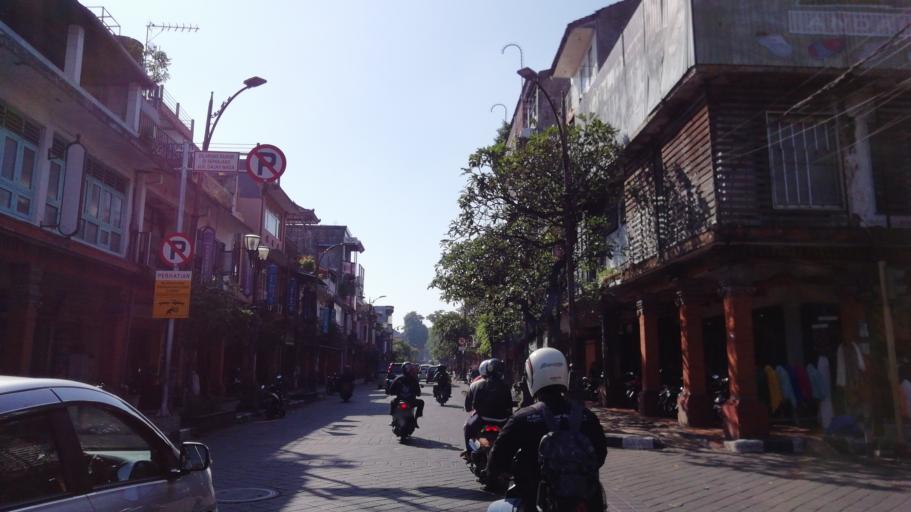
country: ID
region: Bali
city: Denpasar
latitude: -8.6555
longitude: 115.2131
